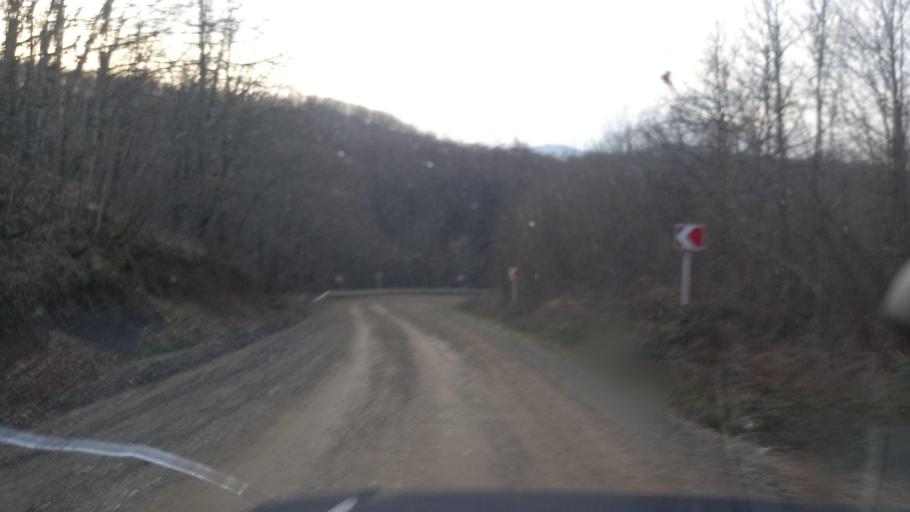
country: RU
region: Krasnodarskiy
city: Goryachiy Klyuch
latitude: 44.3777
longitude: 39.1994
